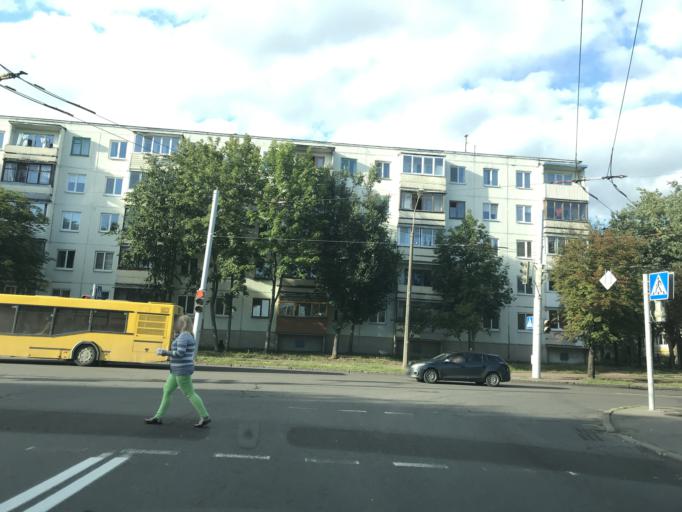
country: BY
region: Minsk
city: Minsk
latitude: 53.9474
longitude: 27.6244
